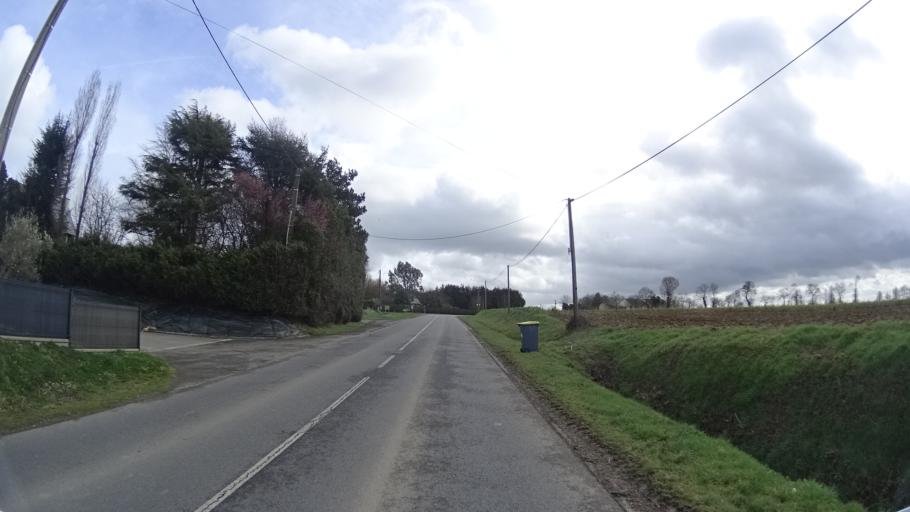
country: FR
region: Brittany
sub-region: Departement d'Ille-et-Vilaine
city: Romille
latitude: 48.2065
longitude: -1.8820
